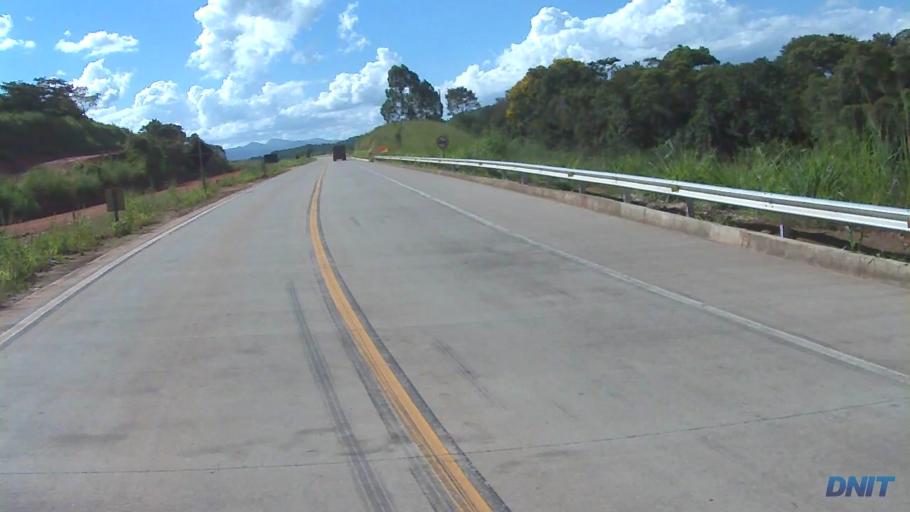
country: BR
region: Minas Gerais
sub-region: Barao De Cocais
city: Barao de Cocais
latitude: -19.7658
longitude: -43.4588
